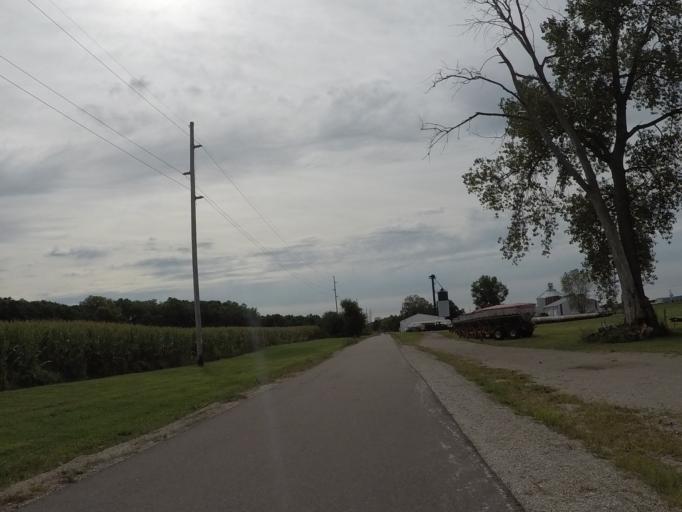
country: US
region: Wisconsin
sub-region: Sauk County
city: Prairie du Sac
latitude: 43.3181
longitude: -89.7391
